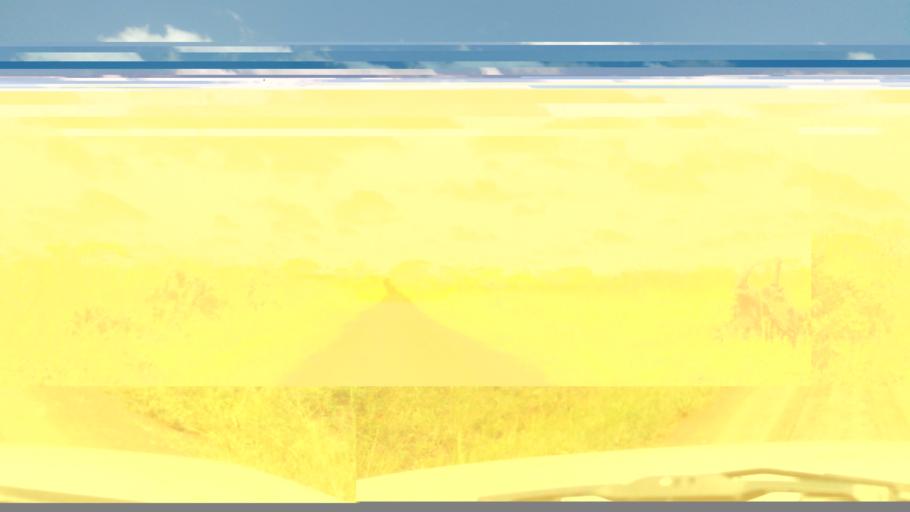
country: UG
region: Western Region
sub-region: Masindi District
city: Masindi
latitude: 1.7389
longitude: 31.8756
